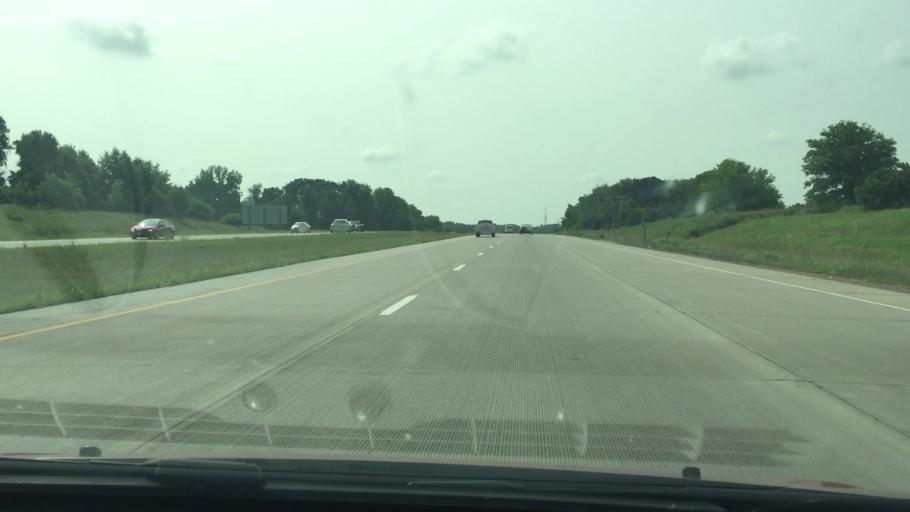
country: US
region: Iowa
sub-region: Scott County
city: Buffalo
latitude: 41.5341
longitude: -90.6759
